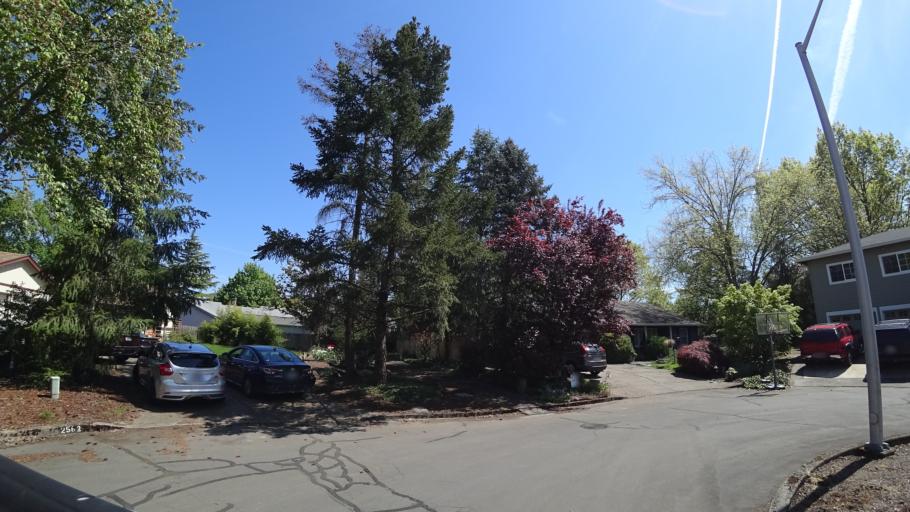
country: US
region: Oregon
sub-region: Washington County
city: Hillsboro
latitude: 45.5003
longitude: -122.9615
